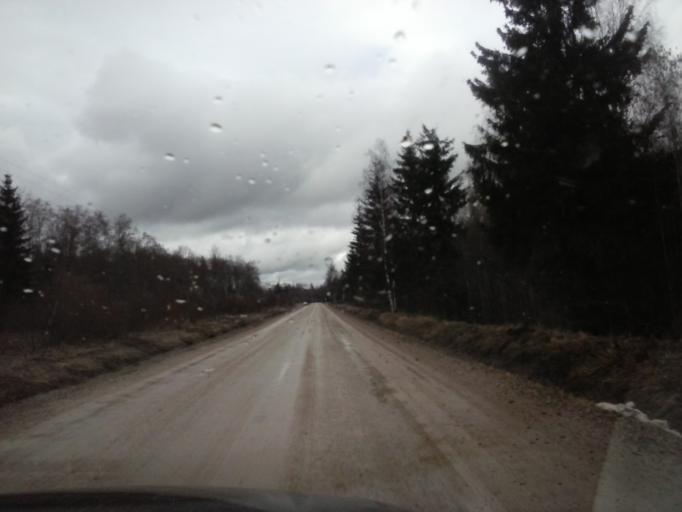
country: EE
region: Ida-Virumaa
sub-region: Kivioli linn
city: Kivioli
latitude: 59.1089
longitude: 26.9212
